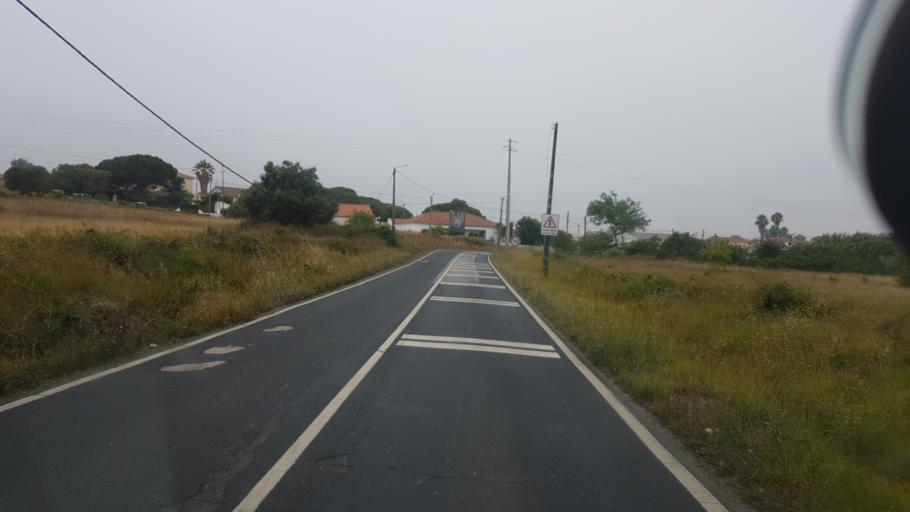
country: PT
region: Lisbon
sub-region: Sintra
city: Sintra
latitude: 38.8290
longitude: -9.3694
